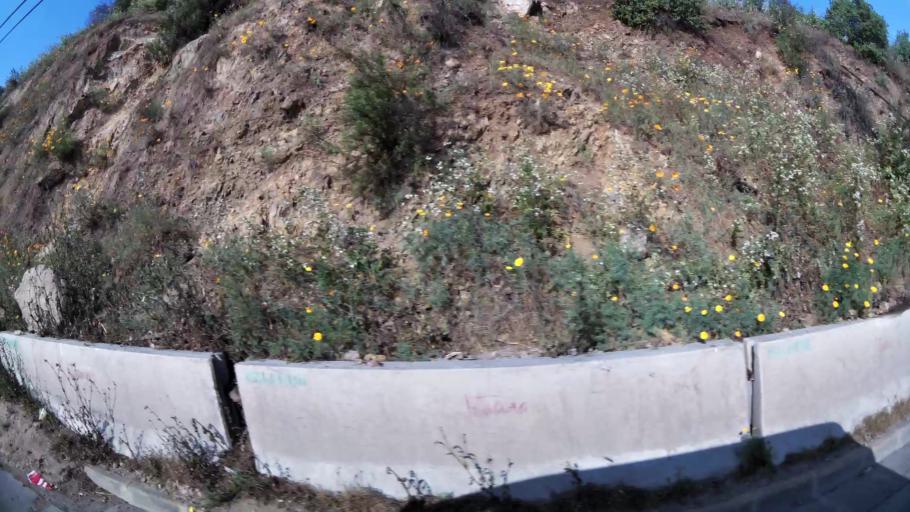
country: CL
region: Santiago Metropolitan
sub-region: Provincia de Santiago
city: Villa Presidente Frei, Nunoa, Santiago, Chile
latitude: -33.3692
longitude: -70.5444
